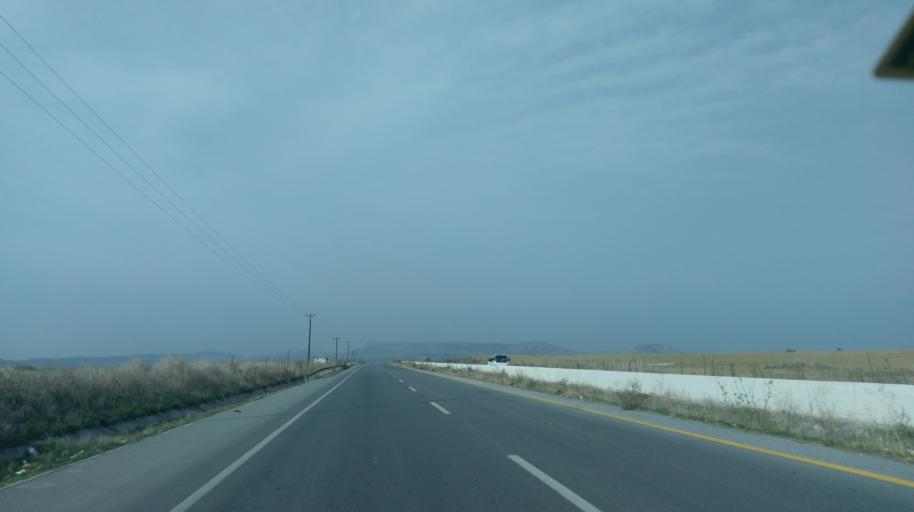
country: CY
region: Lefkosia
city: Mammari
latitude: 35.2120
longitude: 33.2067
